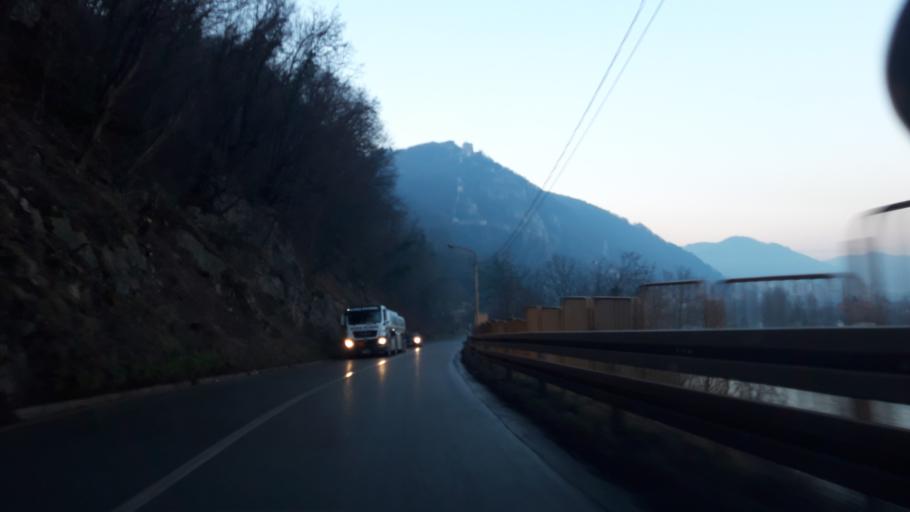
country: RS
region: Central Serbia
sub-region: Macvanski Okrug
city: Mali Zvornik
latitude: 44.3670
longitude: 19.1041
